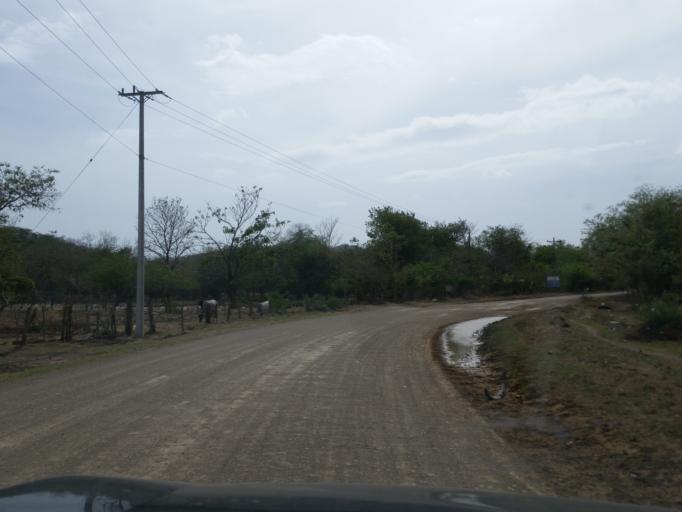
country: NI
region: Rivas
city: Tola
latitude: 11.4476
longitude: -86.0596
